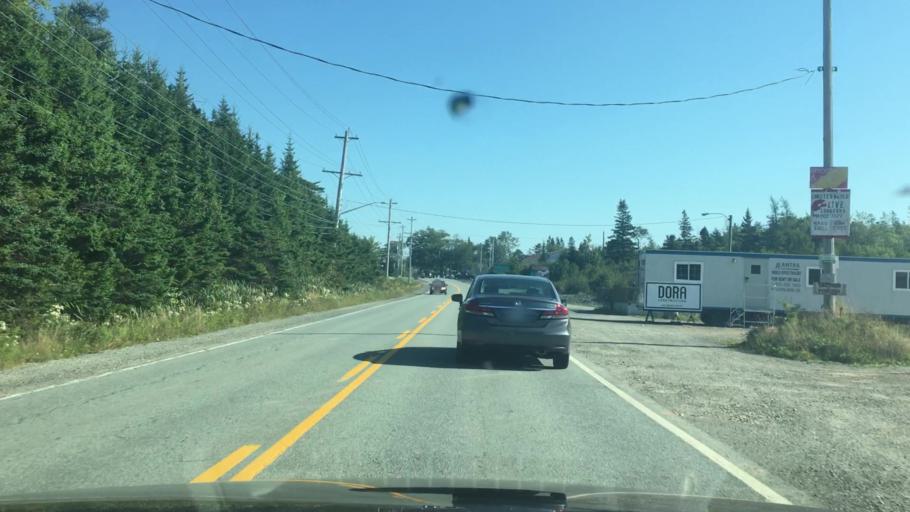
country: CA
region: Nova Scotia
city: Cole Harbour
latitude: 44.7849
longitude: -63.1508
